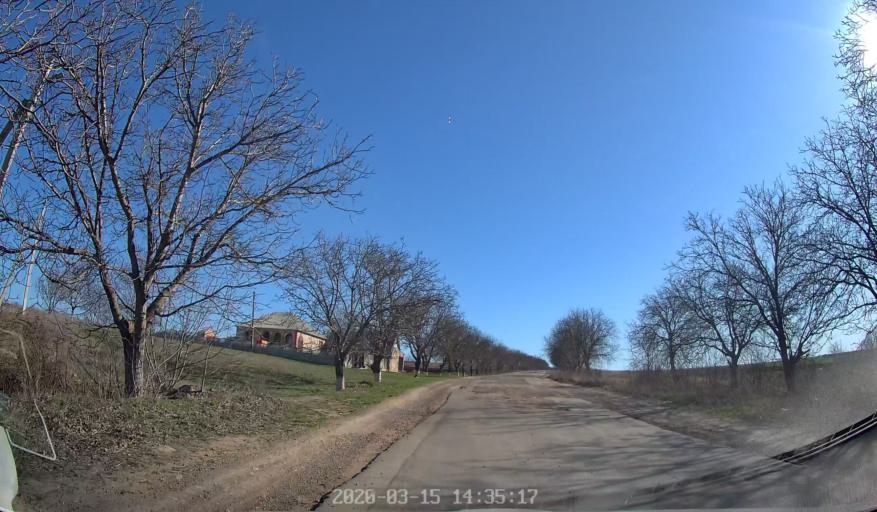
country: MD
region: Orhei
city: Orhei
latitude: 47.3300
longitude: 28.9244
